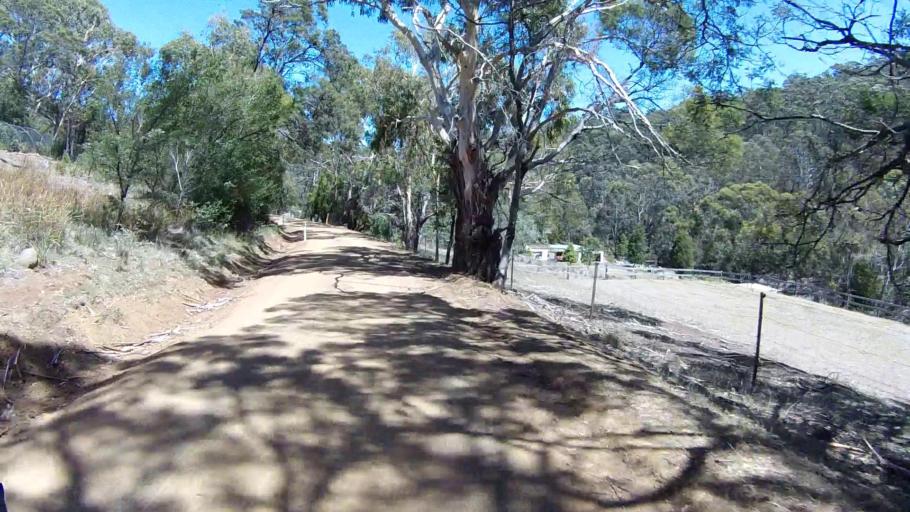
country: AU
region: Tasmania
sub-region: Clarence
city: Cambridge
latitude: -42.8501
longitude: 147.4392
